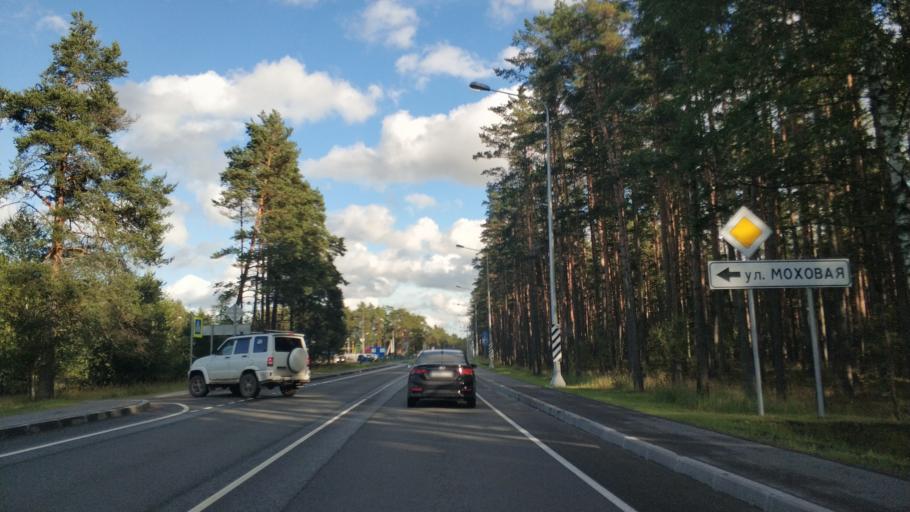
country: RU
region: Leningrad
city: Priozersk
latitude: 61.0164
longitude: 30.1430
